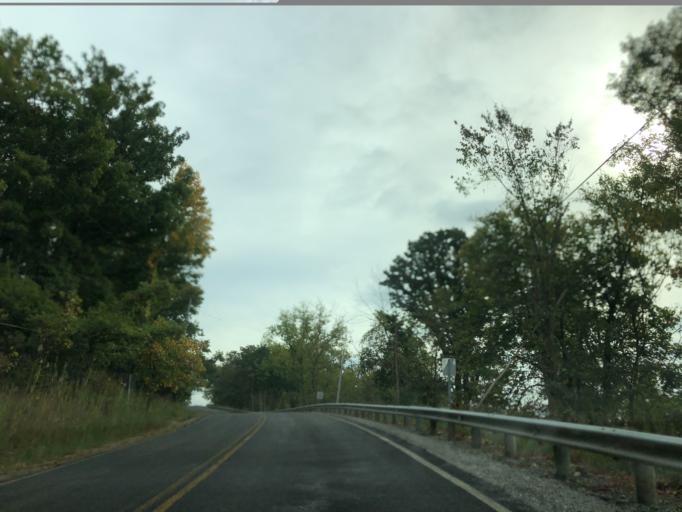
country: US
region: Ohio
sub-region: Summit County
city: Peninsula
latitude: 41.2895
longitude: -81.5586
